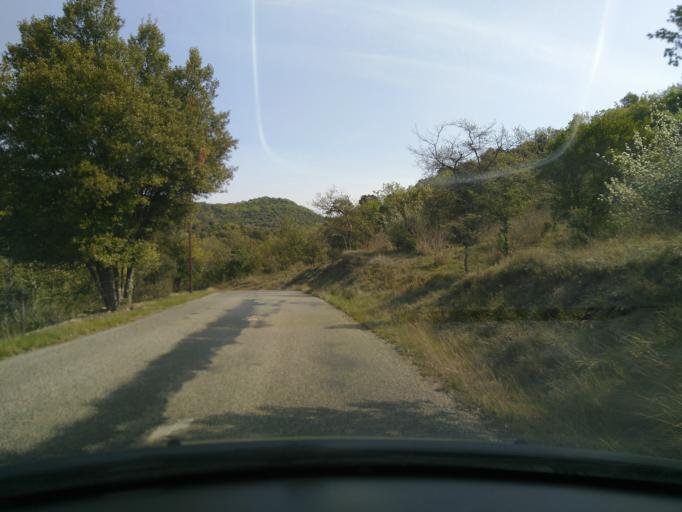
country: FR
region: Rhone-Alpes
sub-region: Departement de l'Ardeche
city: Ruoms
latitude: 44.4517
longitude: 4.3876
